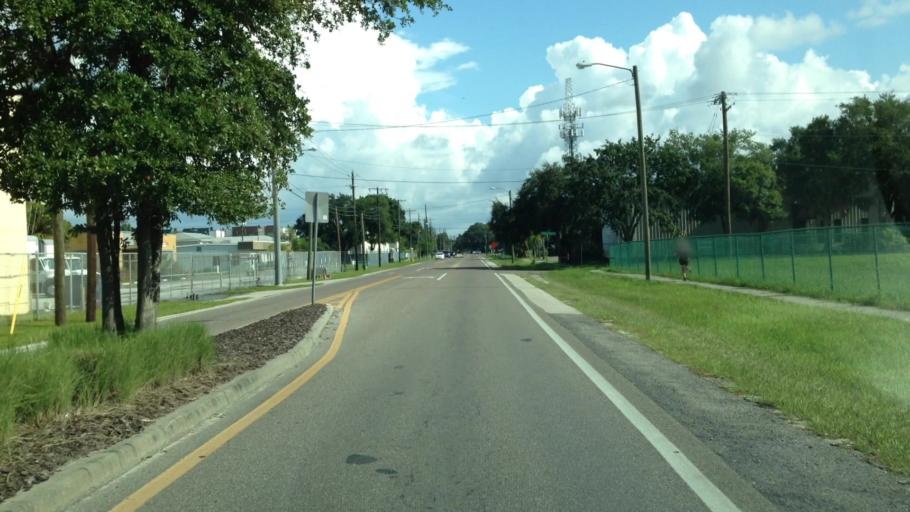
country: US
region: Florida
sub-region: Hillsborough County
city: Tampa
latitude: 27.8890
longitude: -82.5268
